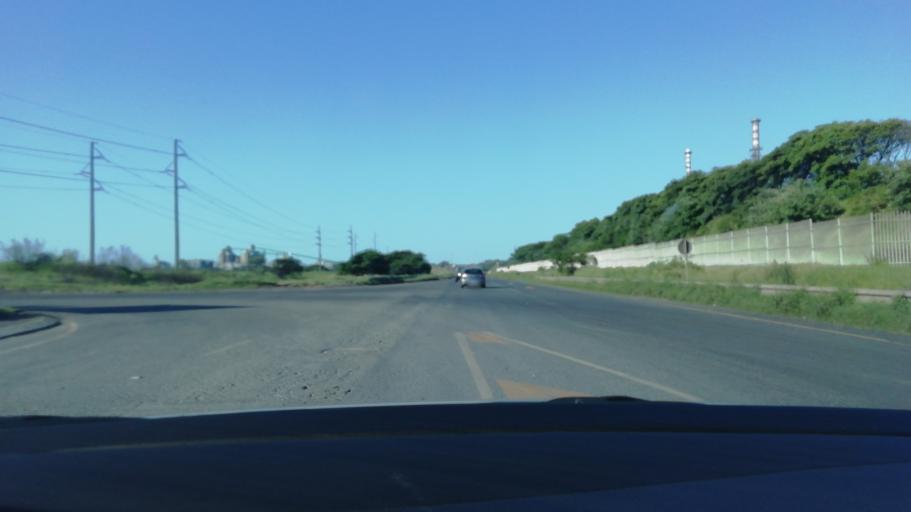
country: ZA
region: KwaZulu-Natal
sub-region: uThungulu District Municipality
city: Richards Bay
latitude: -28.7754
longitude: 32.0316
